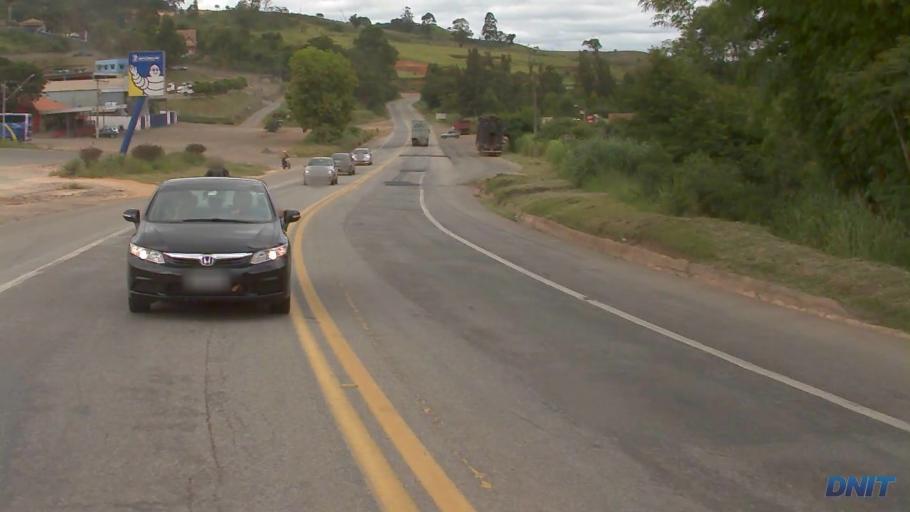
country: BR
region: Minas Gerais
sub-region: Joao Monlevade
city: Joao Monlevade
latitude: -19.8576
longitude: -43.2184
